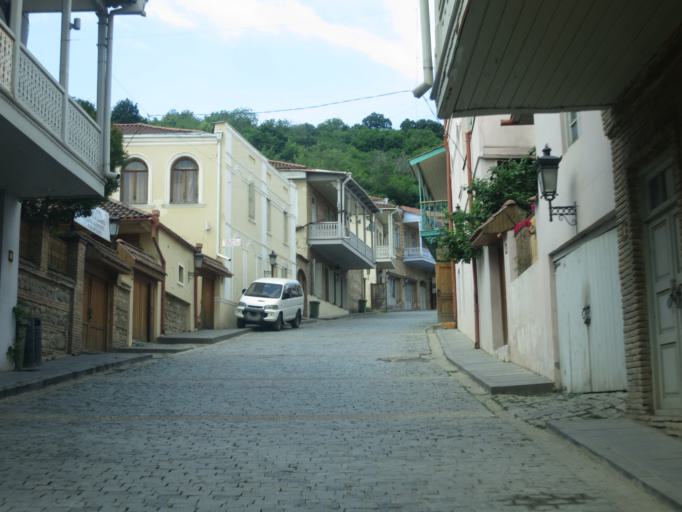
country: GE
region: Kakheti
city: Sighnaghi
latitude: 41.6162
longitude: 45.9202
